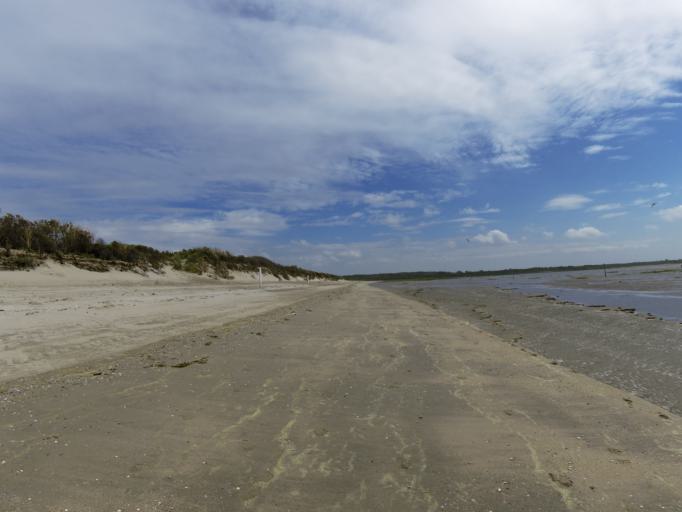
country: NL
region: South Holland
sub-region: Gemeente Rotterdam
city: Hoek van Holland
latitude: 51.9210
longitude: 4.0483
